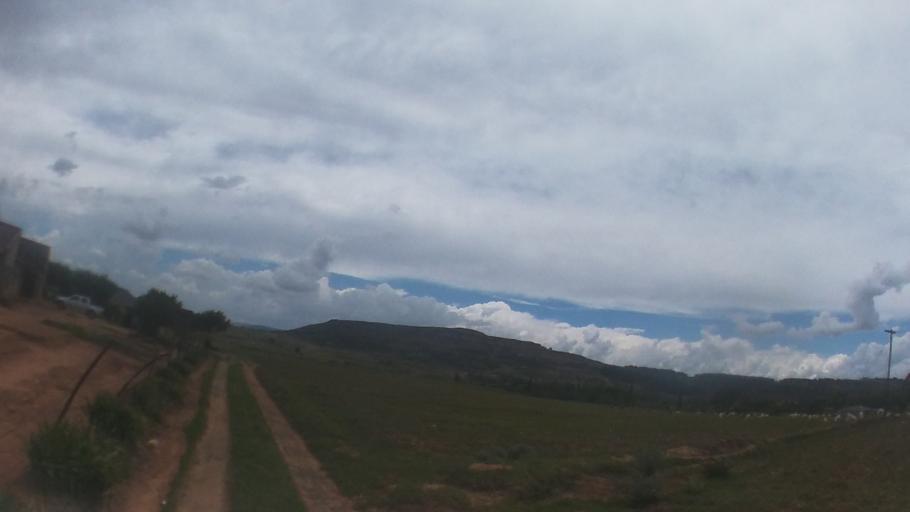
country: LS
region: Maseru
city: Nako
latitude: -29.6220
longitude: 27.5021
